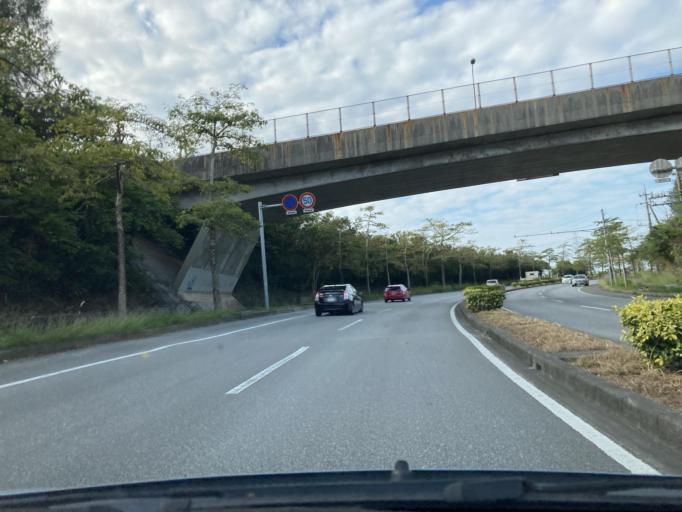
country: JP
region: Okinawa
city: Okinawa
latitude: 26.3171
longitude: 127.7909
